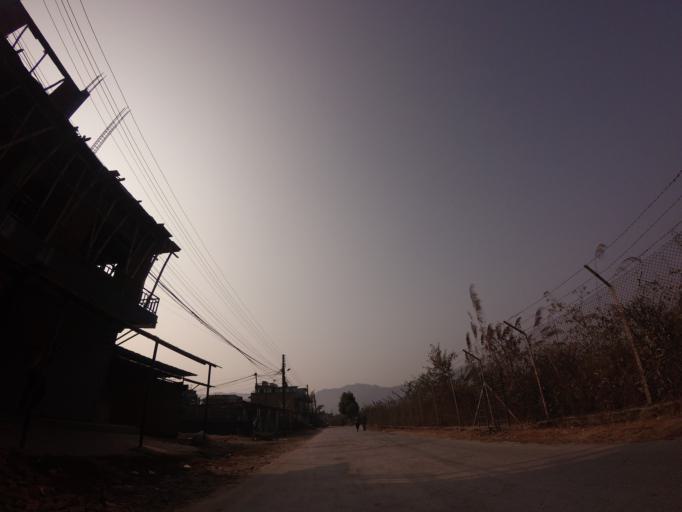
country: NP
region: Western Region
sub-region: Gandaki Zone
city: Pokhara
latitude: 28.1962
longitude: 83.9793
